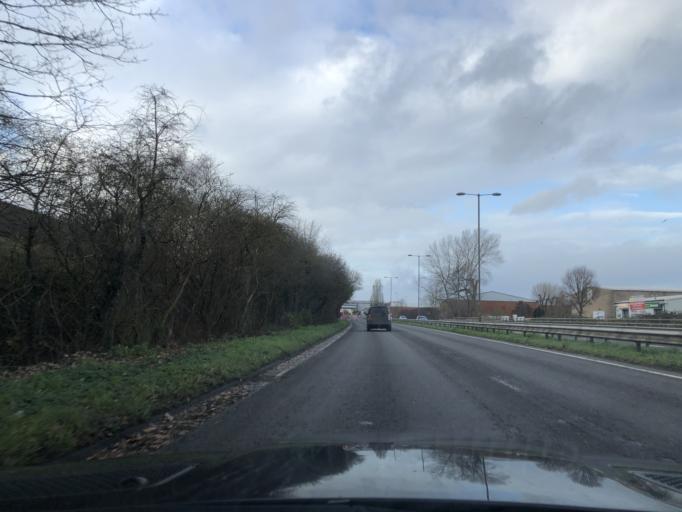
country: GB
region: England
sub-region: Bracknell Forest
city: Sandhurst
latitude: 51.3281
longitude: -0.7688
